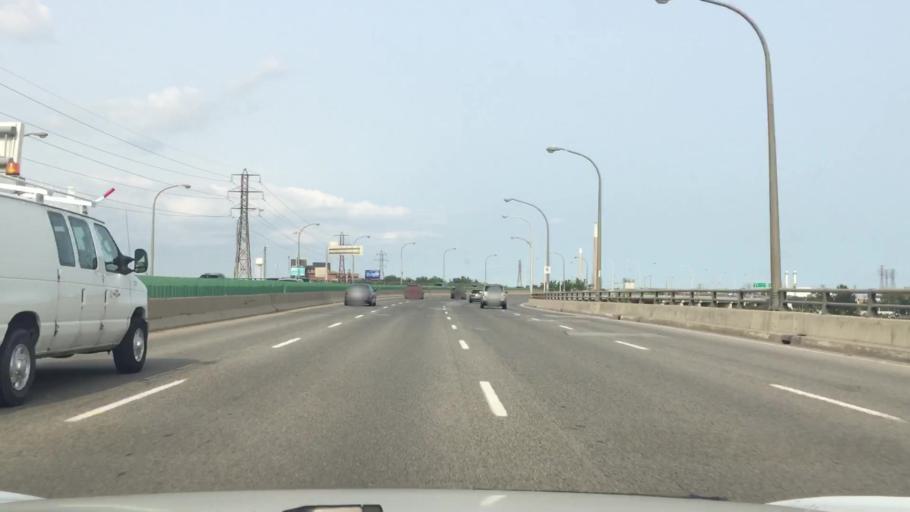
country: CA
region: Ontario
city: Toronto
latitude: 43.6478
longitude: -79.3587
